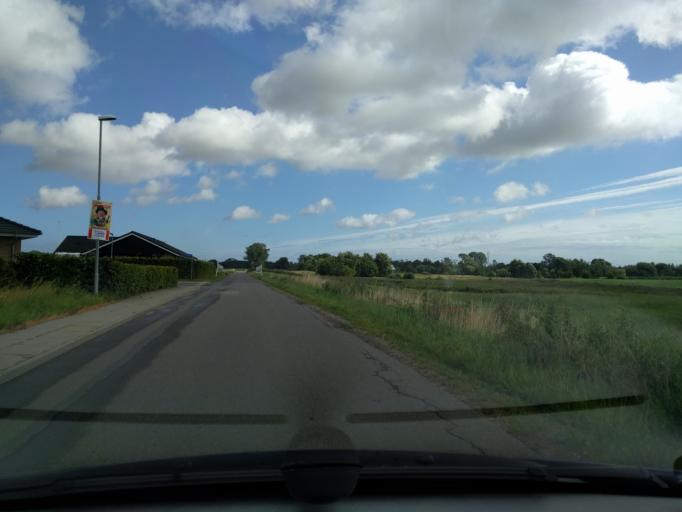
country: DK
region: South Denmark
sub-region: Kerteminde Kommune
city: Langeskov
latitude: 55.3807
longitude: 10.5755
